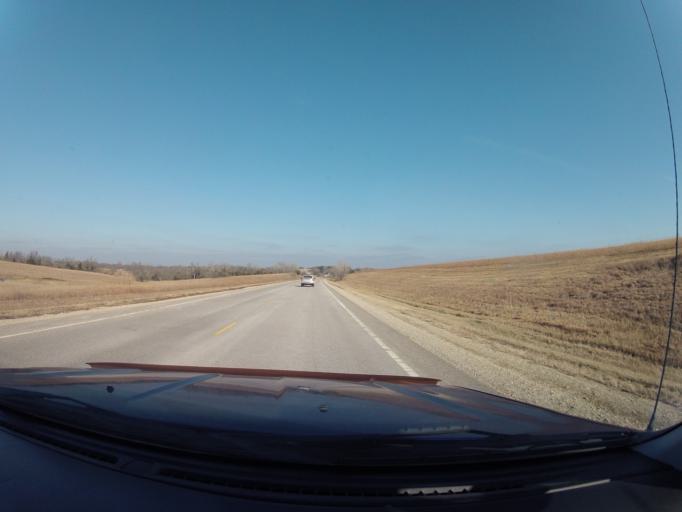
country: US
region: Kansas
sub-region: Marshall County
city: Blue Rapids
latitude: 39.5752
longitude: -96.7504
